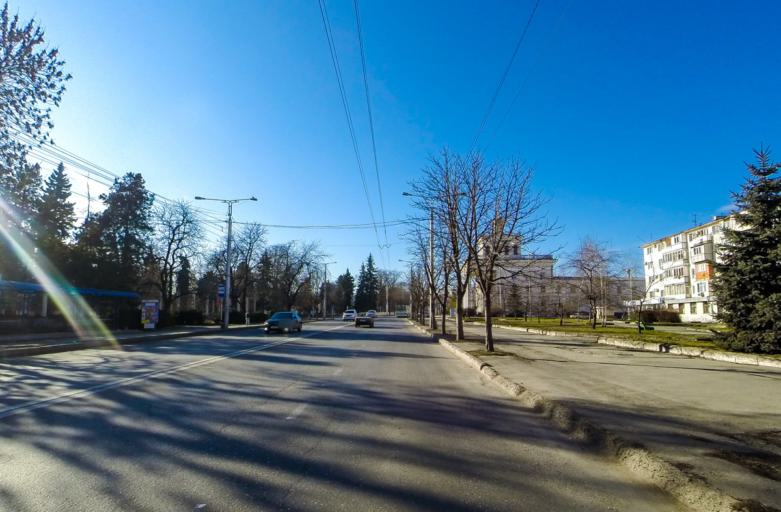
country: RU
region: Kabardino-Balkariya
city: Vol'nyy Aul
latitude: 43.4777
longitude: 43.6024
